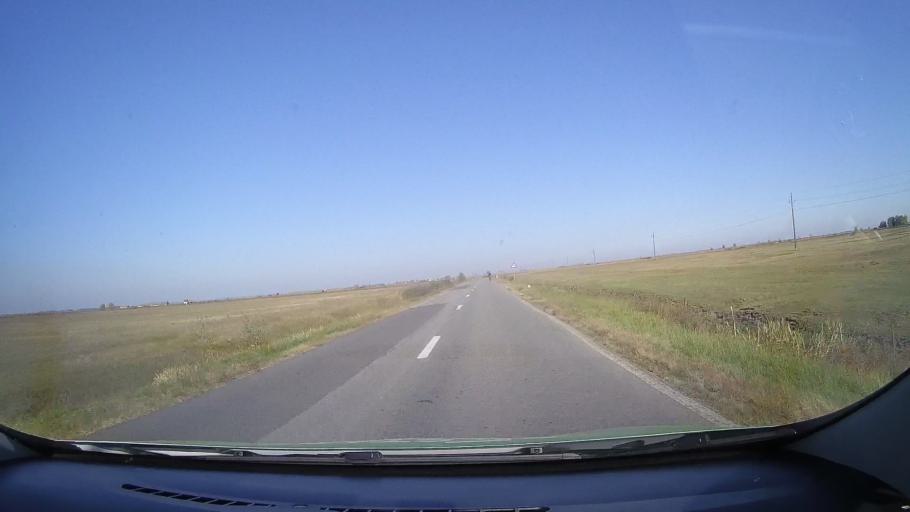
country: RO
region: Satu Mare
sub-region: Comuna Cauas
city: Cauas
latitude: 47.5437
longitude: 22.5634
